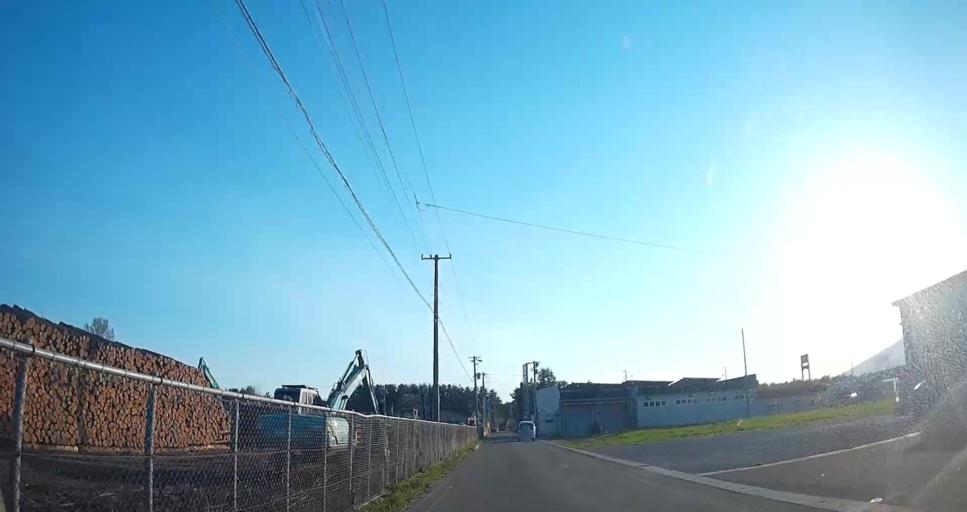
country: JP
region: Aomori
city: Mutsu
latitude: 41.2643
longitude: 141.2171
